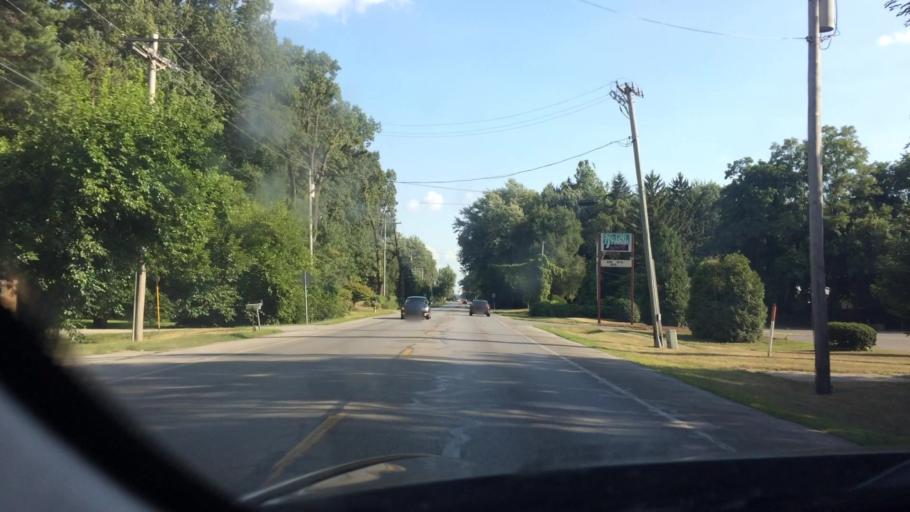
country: US
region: Ohio
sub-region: Lucas County
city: Holland
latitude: 41.6512
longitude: -83.7037
